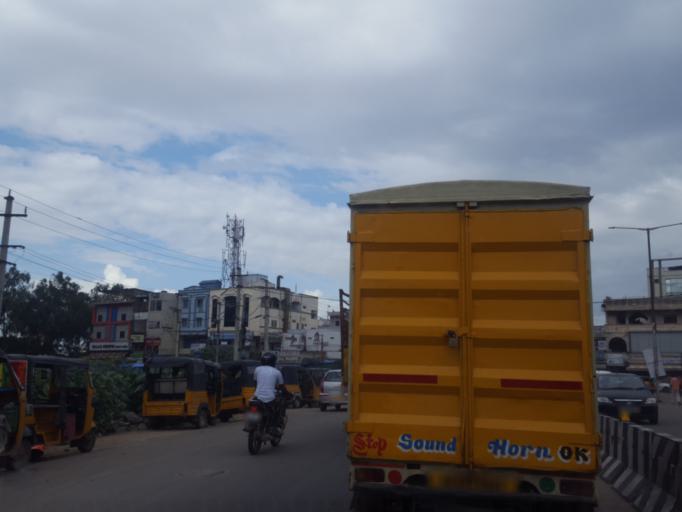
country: IN
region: Telangana
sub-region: Medak
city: Serilingampalle
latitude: 17.4931
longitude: 78.3153
